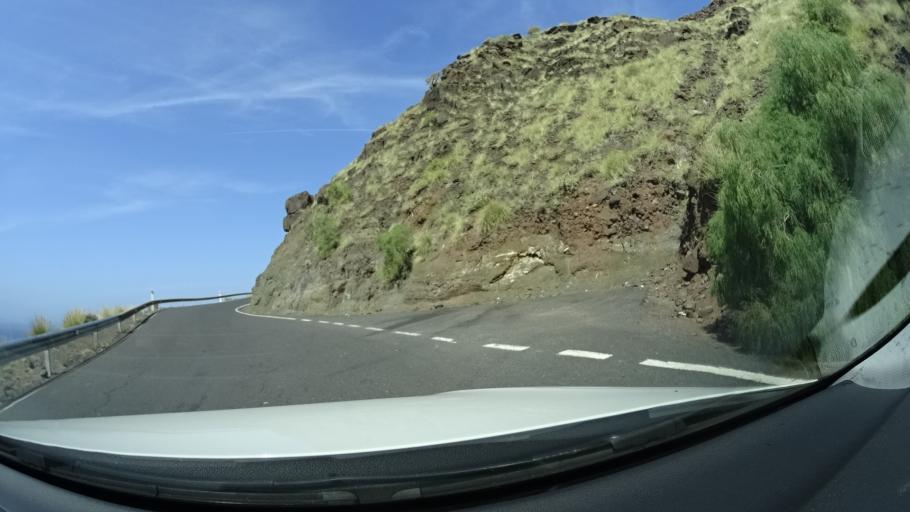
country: ES
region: Canary Islands
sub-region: Provincia de Las Palmas
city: Agaete
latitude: 28.0896
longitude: -15.7035
